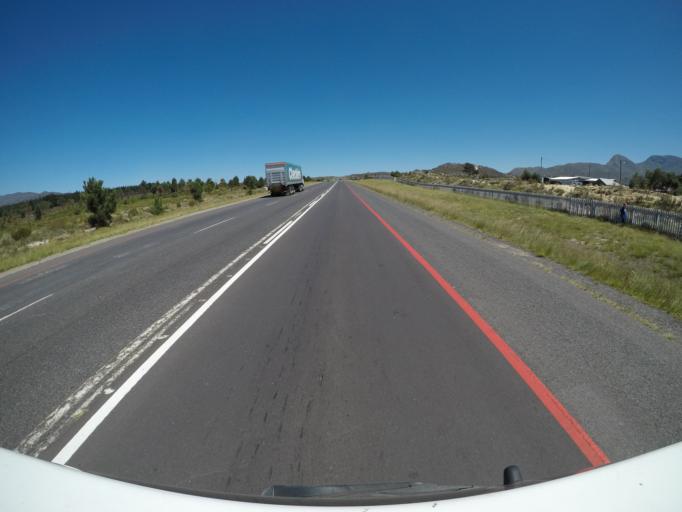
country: ZA
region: Western Cape
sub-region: Overberg District Municipality
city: Grabouw
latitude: -34.1645
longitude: 18.9916
